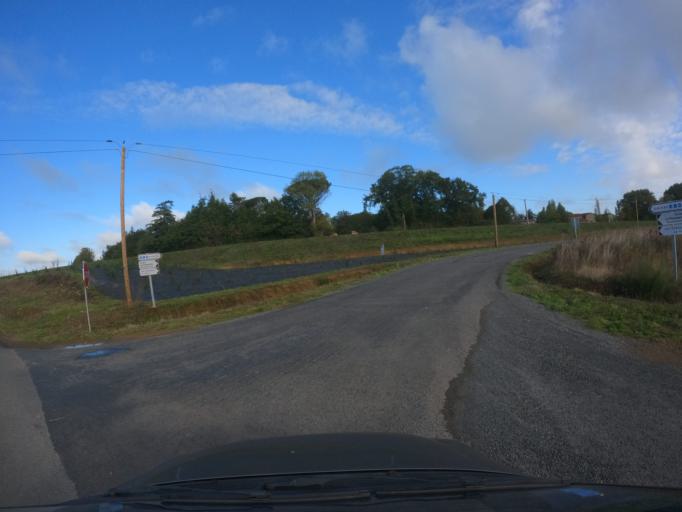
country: FR
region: Pays de la Loire
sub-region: Departement de Maine-et-Loire
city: Vihiers
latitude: 47.1364
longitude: -0.5795
